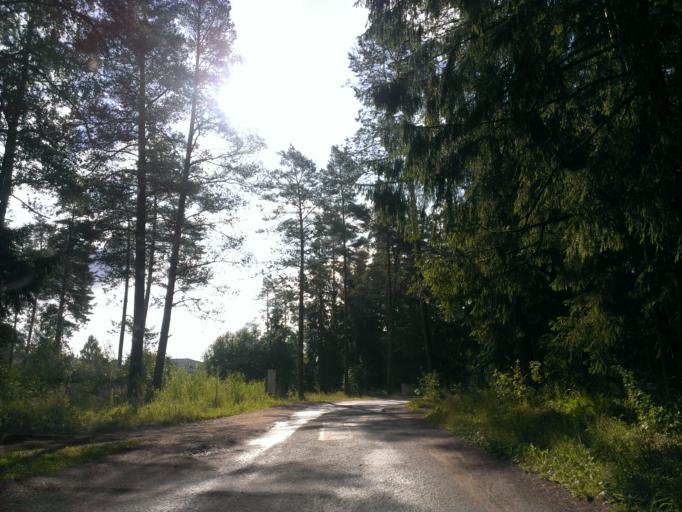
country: LV
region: Incukalns
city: Vangazi
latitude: 57.0960
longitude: 24.5381
